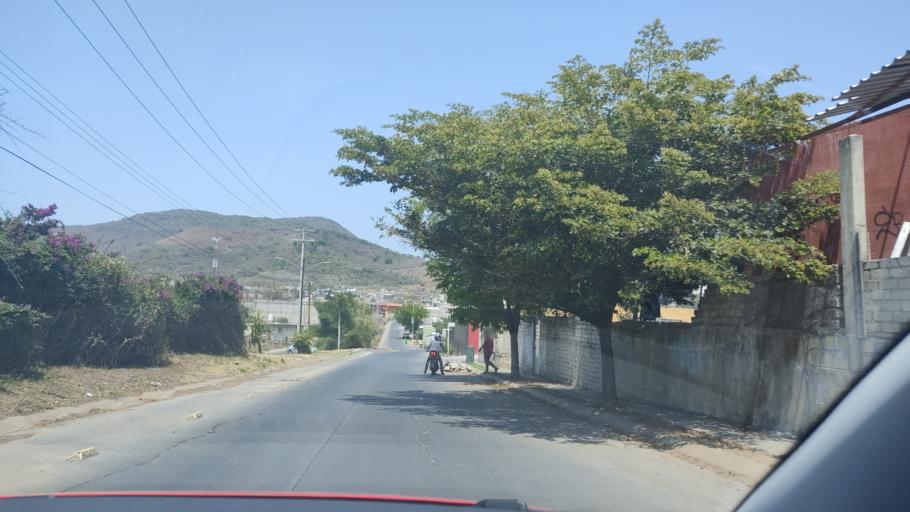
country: MX
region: Nayarit
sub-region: Tepic
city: La Corregidora
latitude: 21.4943
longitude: -104.8215
